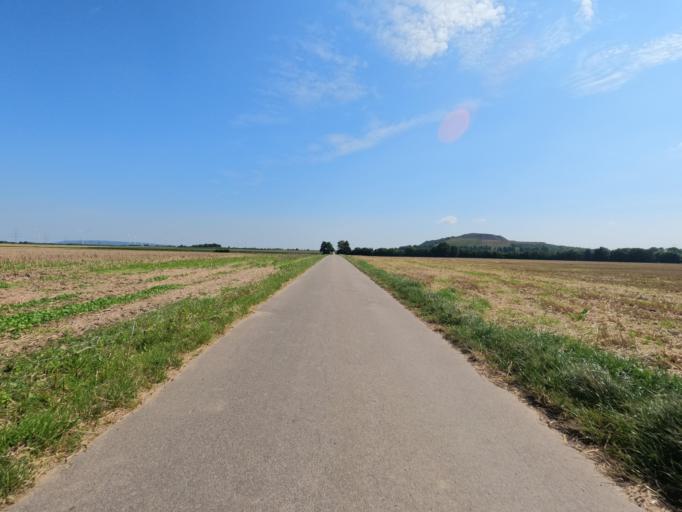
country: DE
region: North Rhine-Westphalia
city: Baesweiler
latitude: 50.9392
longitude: 6.2173
